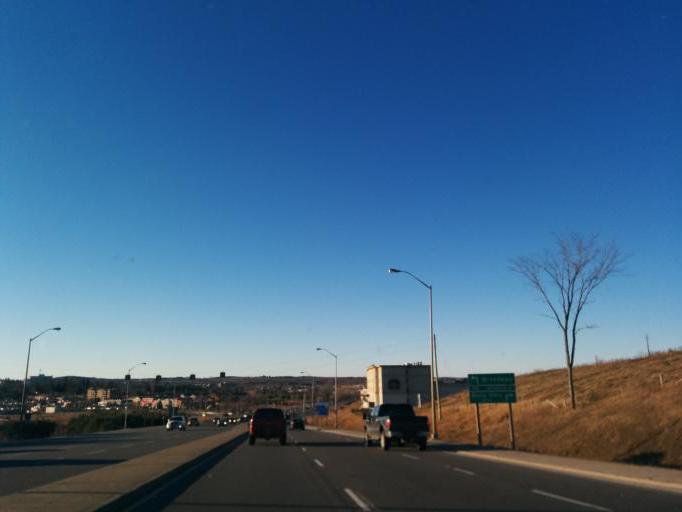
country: CA
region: Ontario
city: Orangeville
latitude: 43.9198
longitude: -80.0784
